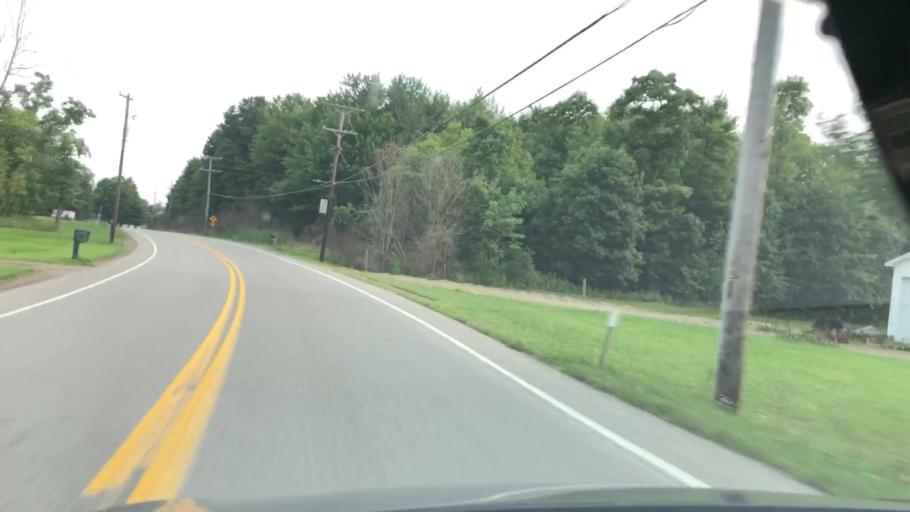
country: US
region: Pennsylvania
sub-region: Crawford County
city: Titusville
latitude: 41.5539
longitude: -79.6990
